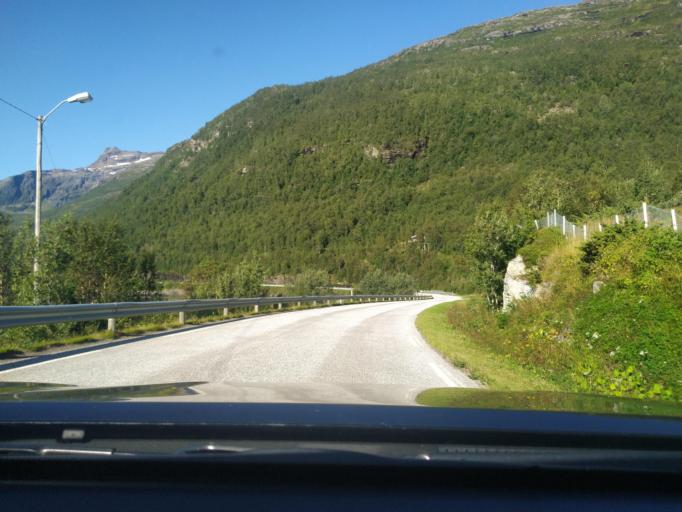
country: NO
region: Troms
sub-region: Dyroy
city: Brostadbotn
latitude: 68.9334
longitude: 17.7032
